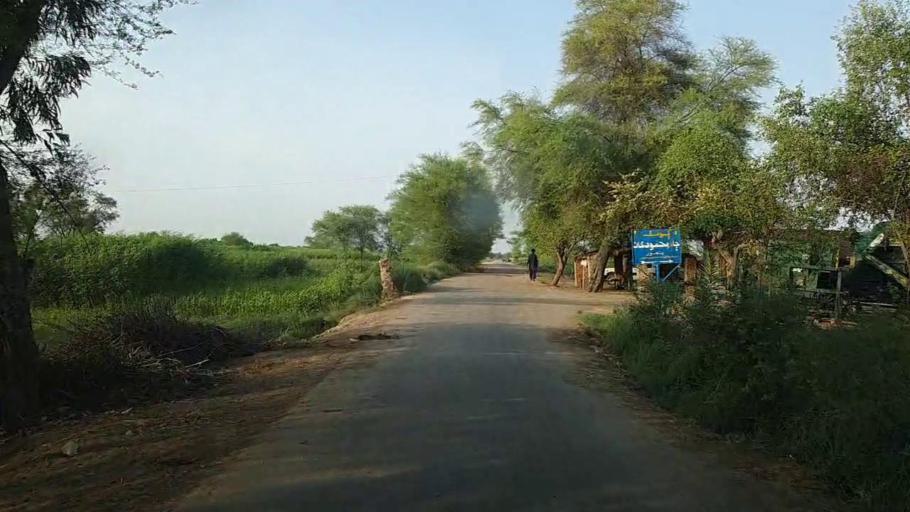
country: PK
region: Sindh
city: Ubauro
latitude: 28.1184
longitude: 69.8243
